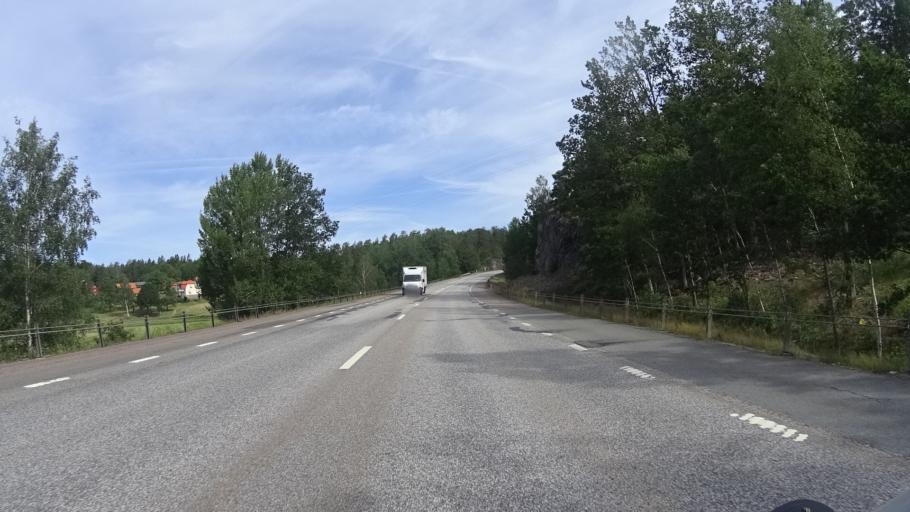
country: SE
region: Kalmar
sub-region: Vasterviks Kommun
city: Ankarsrum
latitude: 57.6648
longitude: 16.4427
